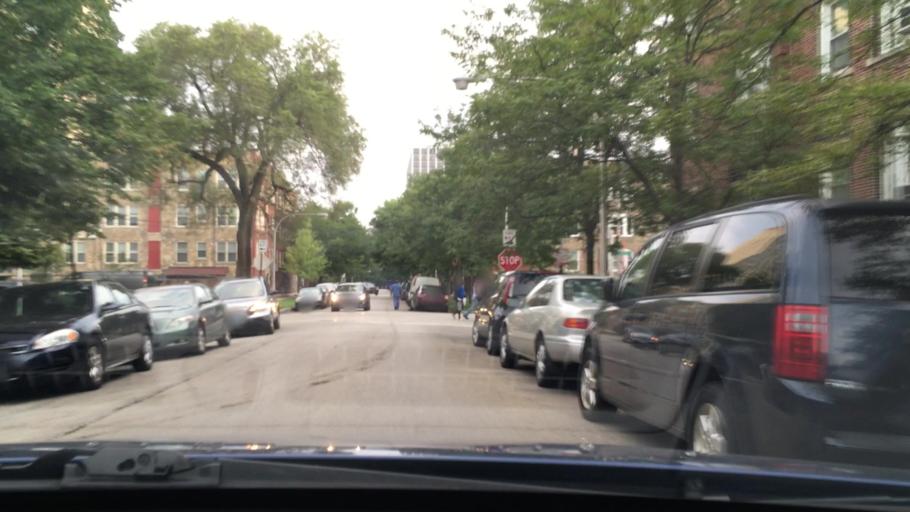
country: US
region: Illinois
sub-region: Cook County
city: Evanston
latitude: 41.9648
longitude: -87.6524
